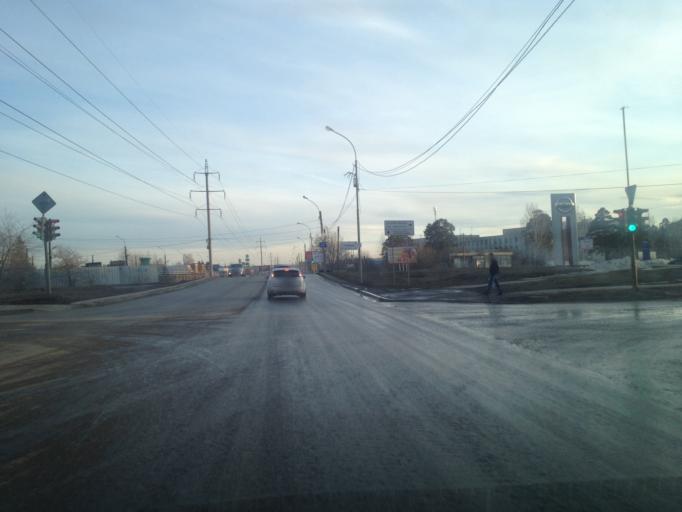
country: RU
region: Sverdlovsk
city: Sovkhoznyy
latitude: 56.7657
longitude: 60.5928
